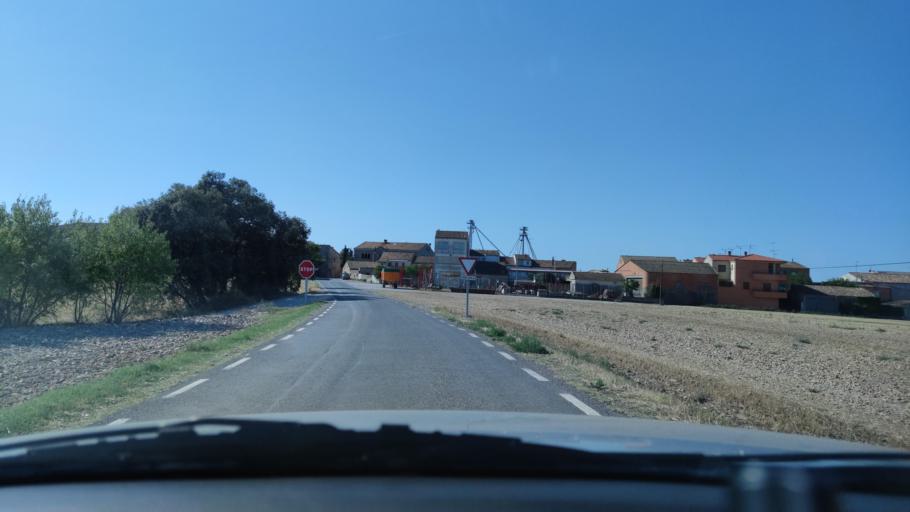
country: ES
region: Catalonia
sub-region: Provincia de Lleida
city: Ivorra
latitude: 41.7278
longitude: 1.3671
